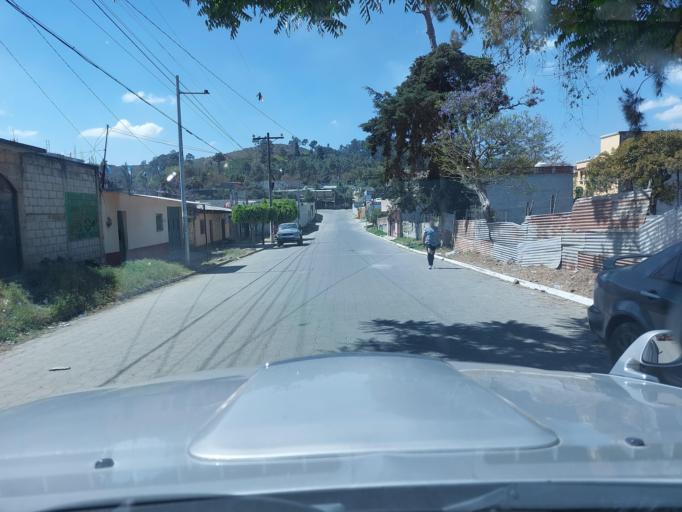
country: GT
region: Chimaltenango
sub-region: Municipio de Chimaltenango
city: Chimaltenango
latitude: 14.6576
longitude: -90.8292
